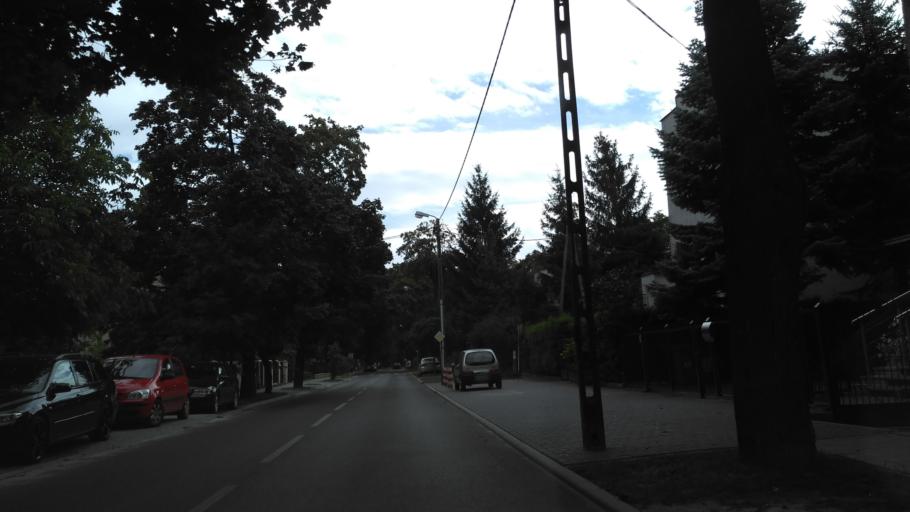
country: PL
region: Lublin Voivodeship
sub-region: Powiat lubelski
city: Lublin
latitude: 51.2169
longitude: 22.5731
